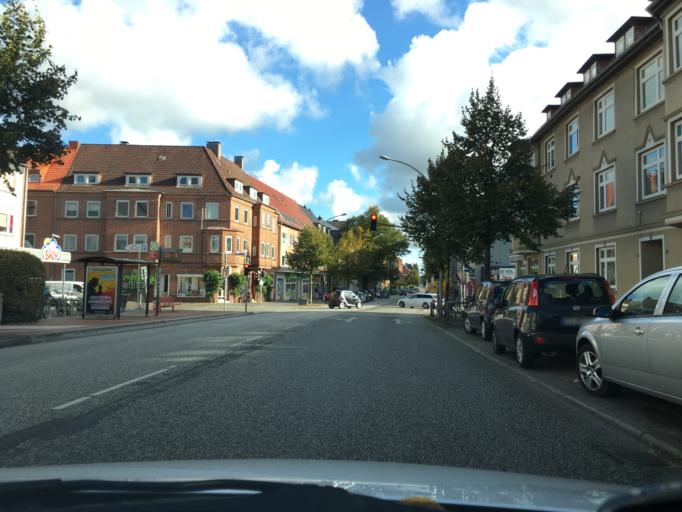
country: DE
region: Schleswig-Holstein
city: Kiel
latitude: 54.3033
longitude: 10.1117
